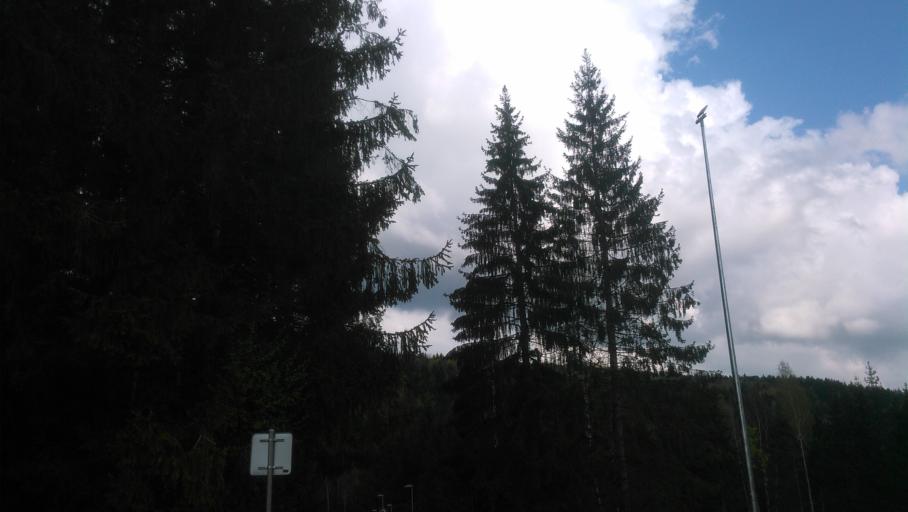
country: SK
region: Banskobystricky
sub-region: Okres Banska Bystrica
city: Brezno
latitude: 48.8643
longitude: 19.6007
